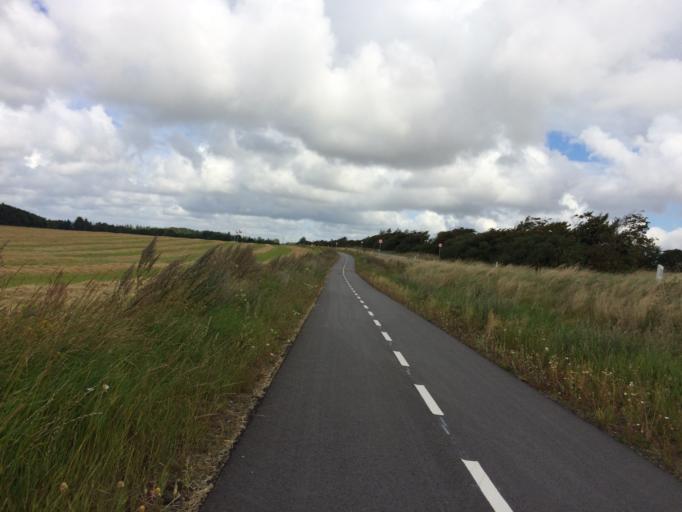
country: DK
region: Central Jutland
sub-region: Holstebro Kommune
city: Ulfborg
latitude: 56.3239
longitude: 8.3422
